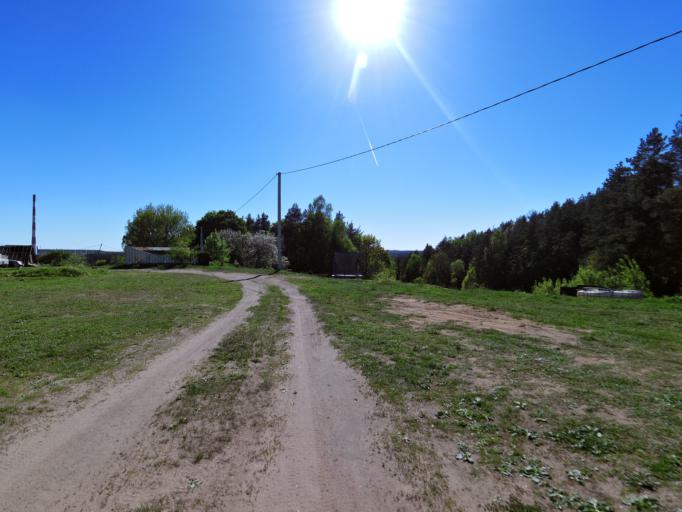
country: LT
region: Vilnius County
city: Pilaite
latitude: 54.6831
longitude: 25.1623
